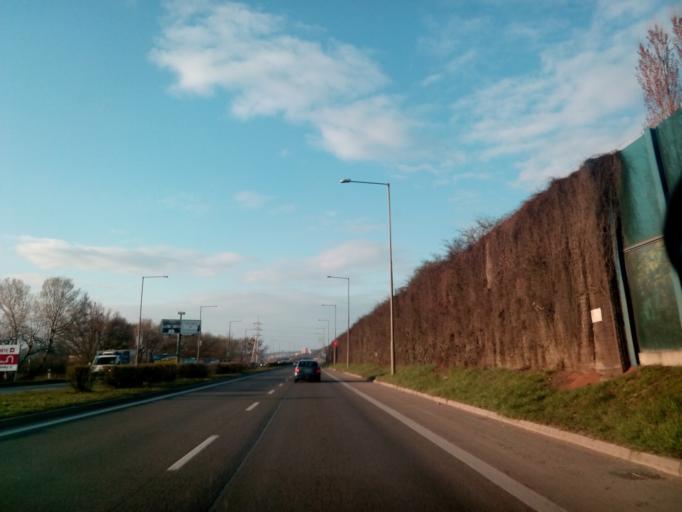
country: SK
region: Kosicky
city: Kosice
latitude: 48.6950
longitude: 21.2803
